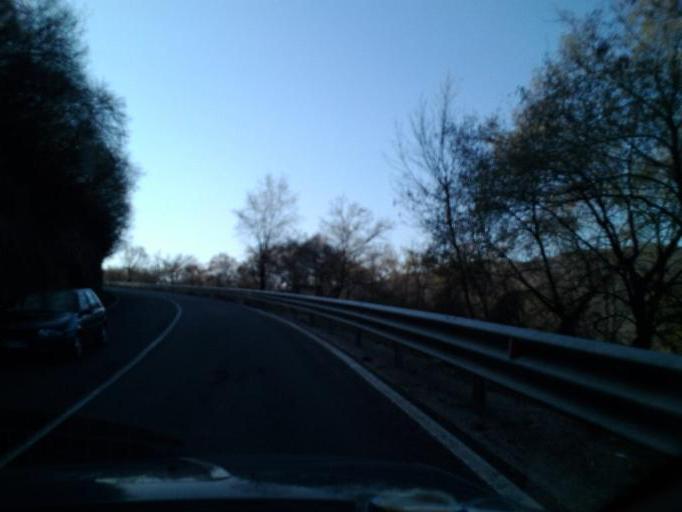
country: IT
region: Veneto
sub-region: Provincia di Verona
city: Grezzana
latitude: 45.5427
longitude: 11.0087
